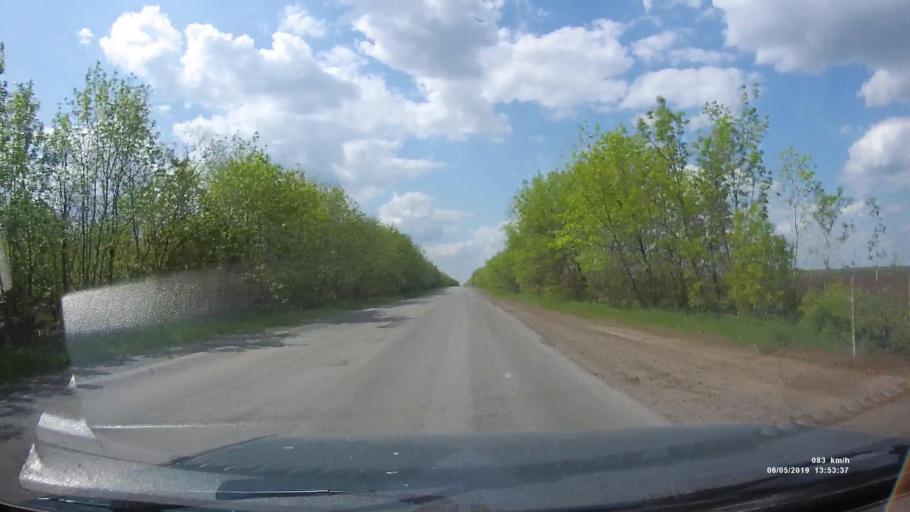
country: RU
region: Rostov
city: Melikhovskaya
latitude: 47.6693
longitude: 40.4598
